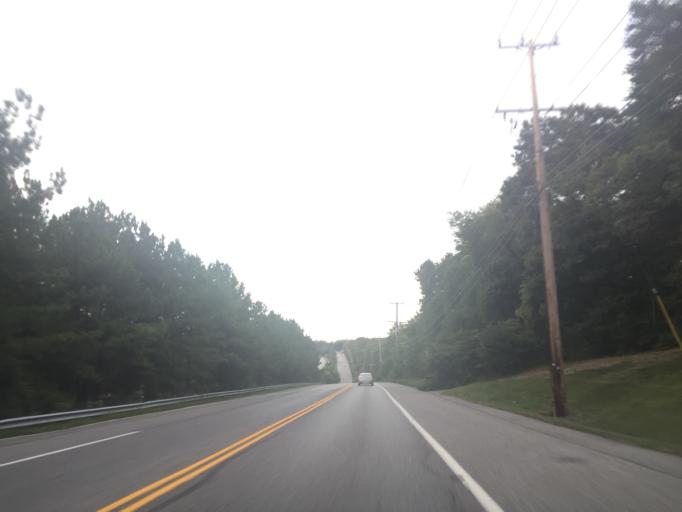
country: US
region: Maryland
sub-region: Anne Arundel County
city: Gambrills
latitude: 39.0763
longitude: -76.6286
